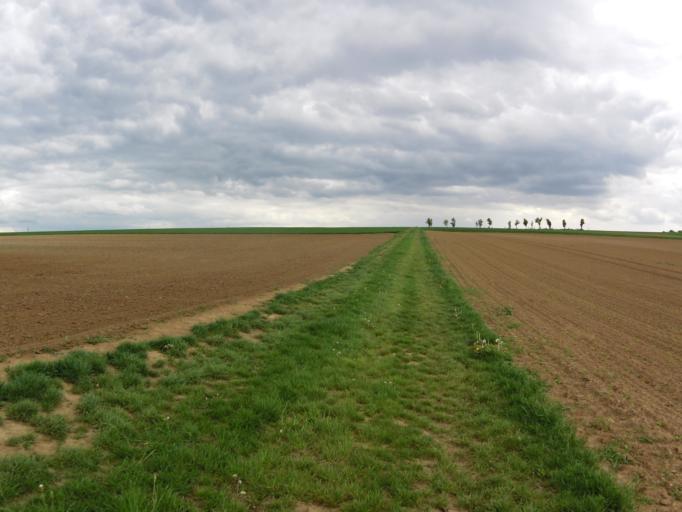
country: DE
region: Bavaria
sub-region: Regierungsbezirk Unterfranken
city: Oberpleichfeld
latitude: 49.8549
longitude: 10.0768
